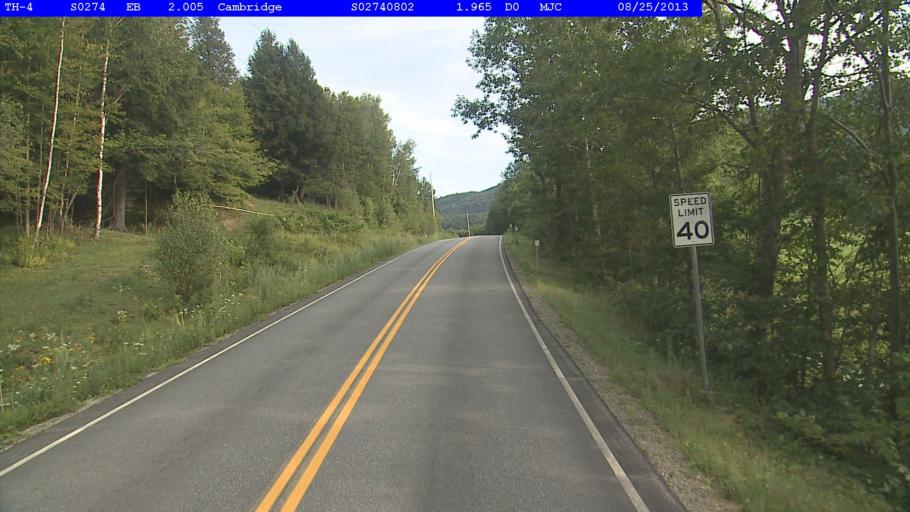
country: US
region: Vermont
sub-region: Lamoille County
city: Johnson
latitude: 44.6589
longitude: -72.7538
